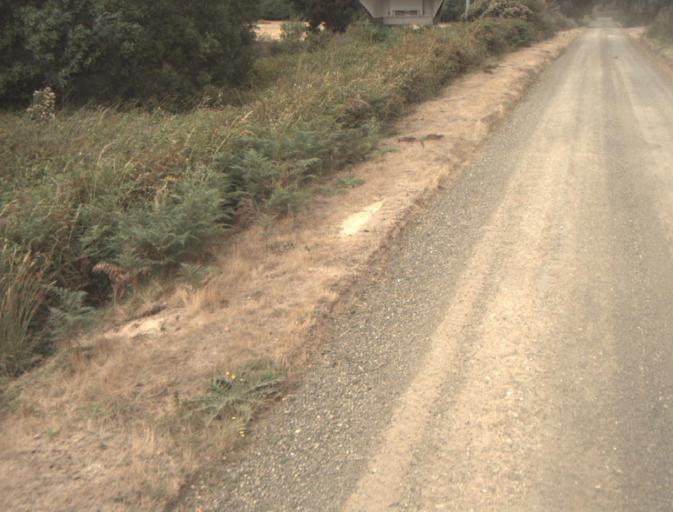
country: AU
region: Tasmania
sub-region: Dorset
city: Bridport
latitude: -41.1912
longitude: 147.2622
